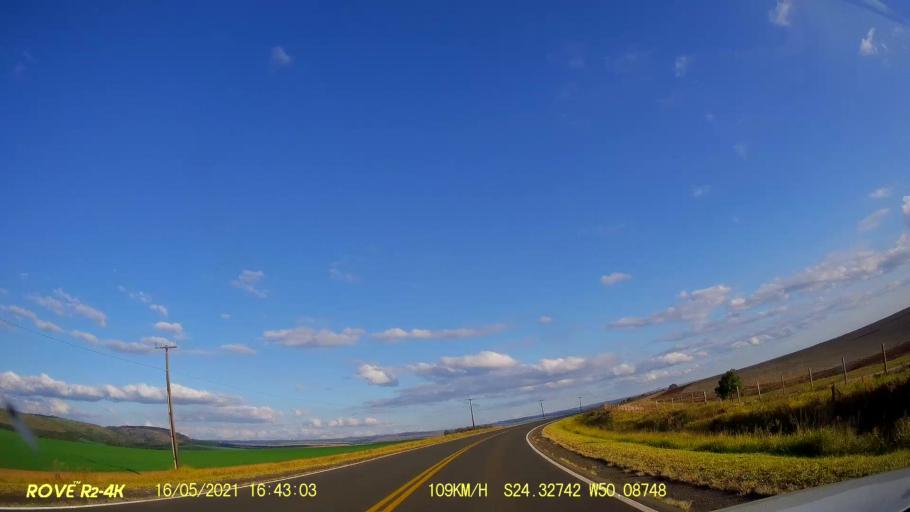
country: BR
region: Parana
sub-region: Pirai Do Sul
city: Pirai do Sul
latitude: -24.3278
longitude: -50.0876
